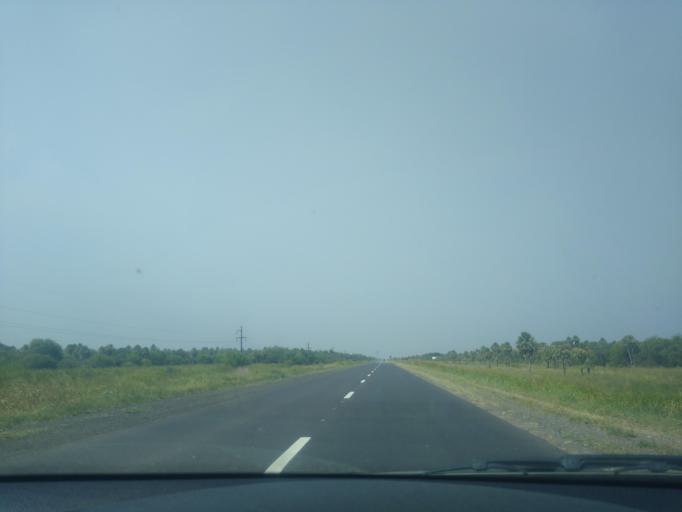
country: AR
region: Chaco
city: Fontana
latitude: -27.5162
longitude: -59.1019
